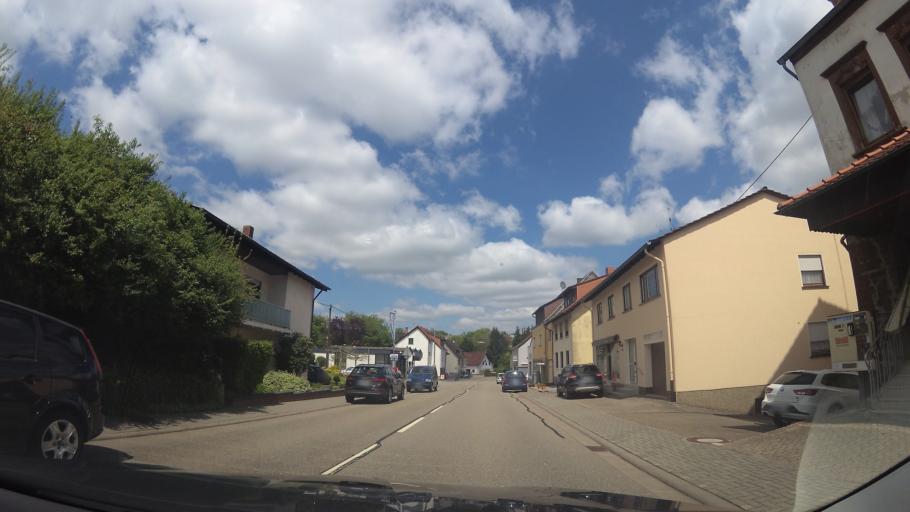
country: DE
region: Saarland
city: Eppelborn
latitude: 49.4328
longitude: 6.9493
